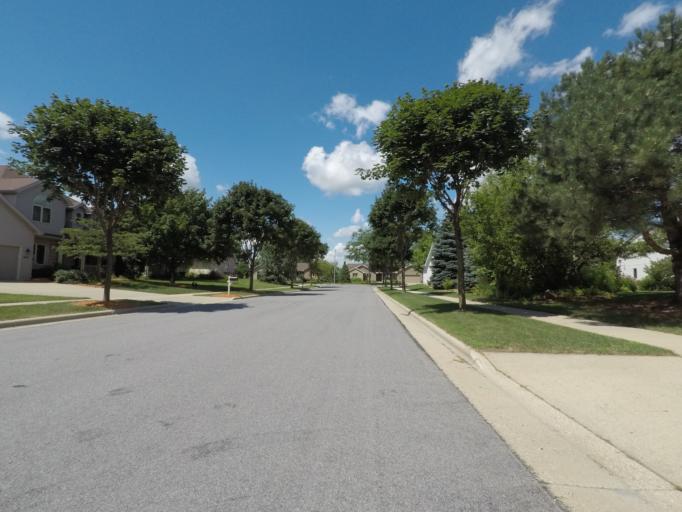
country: US
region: Wisconsin
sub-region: Dane County
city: Middleton
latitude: 43.0701
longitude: -89.5299
